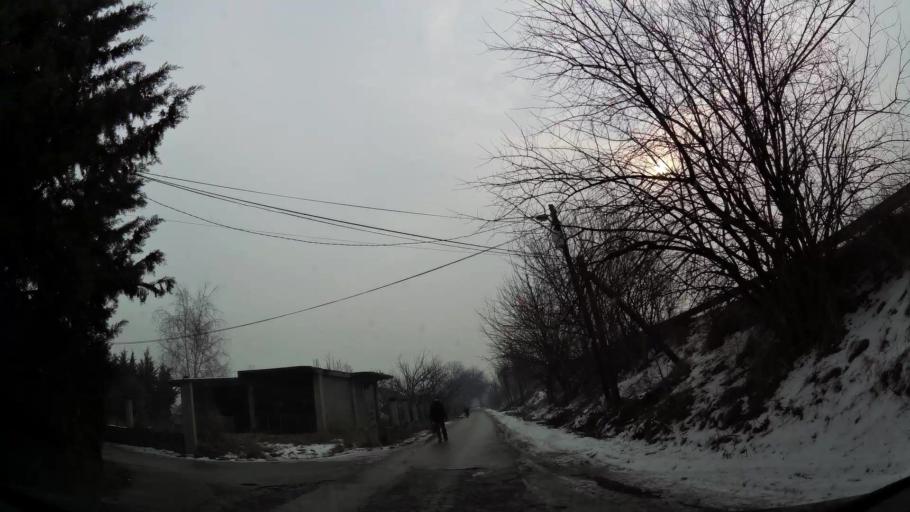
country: MK
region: Ilinden
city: Jurumleri
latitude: 41.9714
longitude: 21.5432
